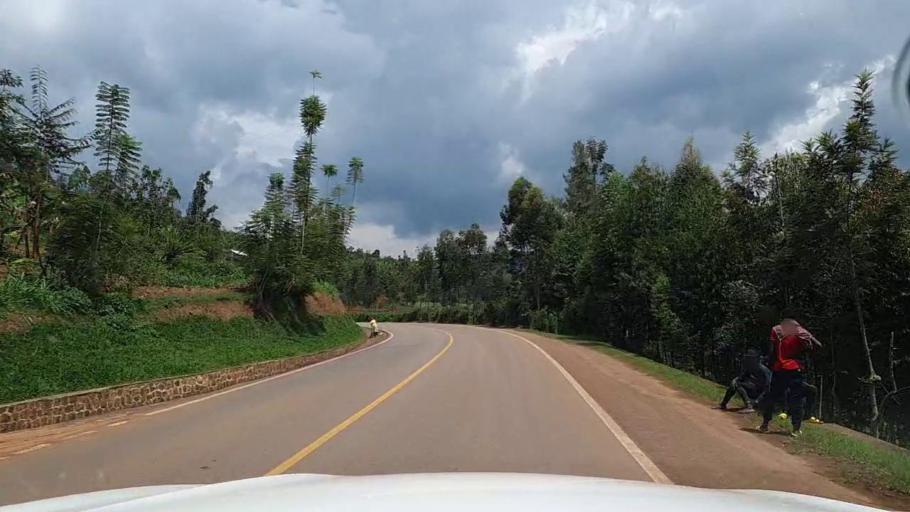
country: RW
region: Kigali
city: Kigali
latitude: -1.8064
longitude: 30.1258
